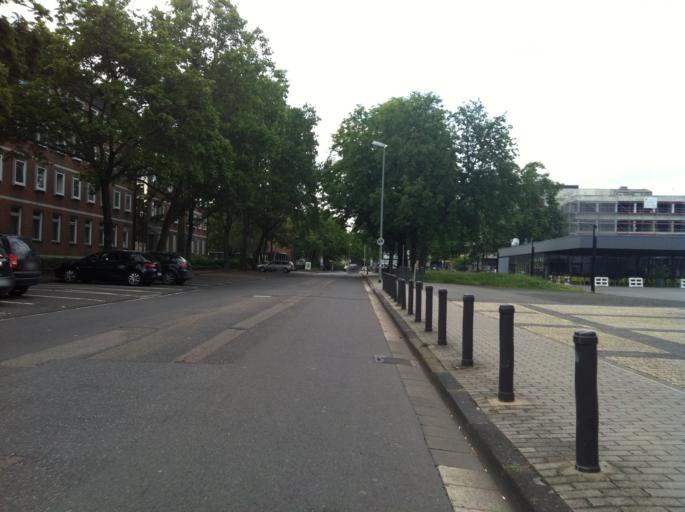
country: DE
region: Rheinland-Pfalz
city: Mainz
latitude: 50.0056
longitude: 8.2444
